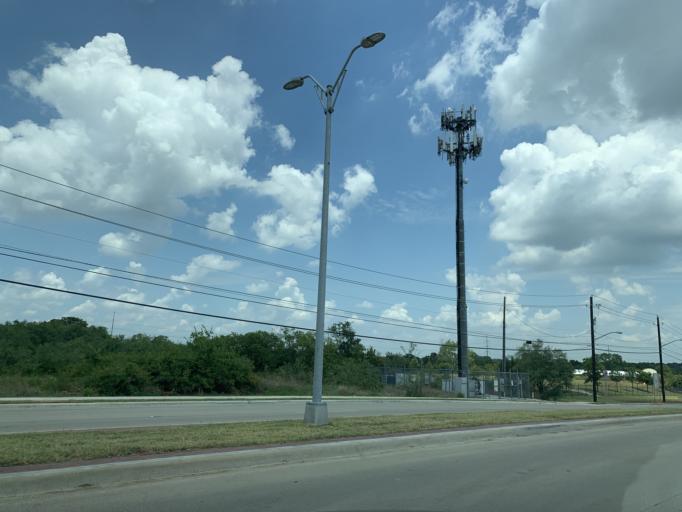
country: US
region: Texas
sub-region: Tarrant County
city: Forest Hill
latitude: 32.7311
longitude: -97.2513
